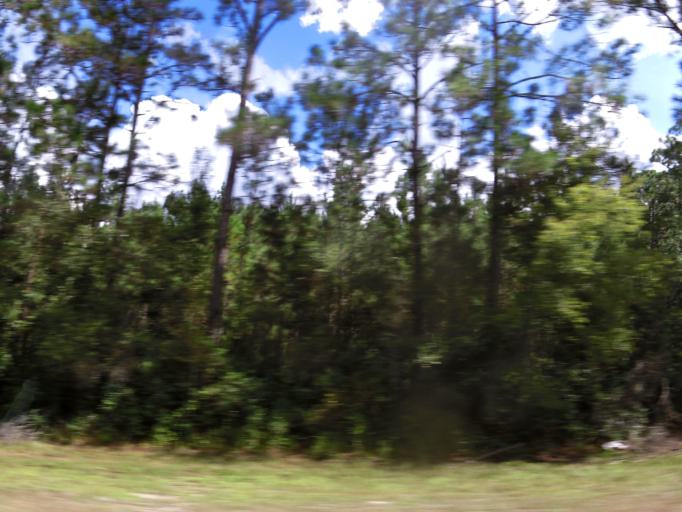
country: US
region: Georgia
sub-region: Charlton County
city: Folkston
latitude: 30.9472
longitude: -82.0228
